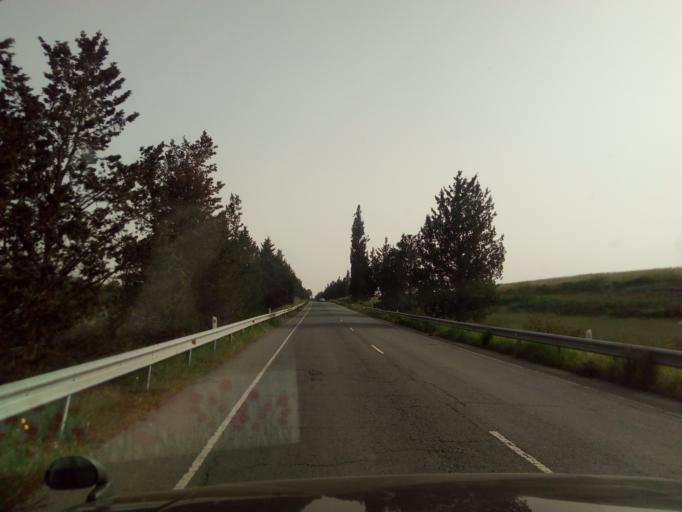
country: CY
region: Lefkosia
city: Lympia
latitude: 35.0213
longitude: 33.4947
